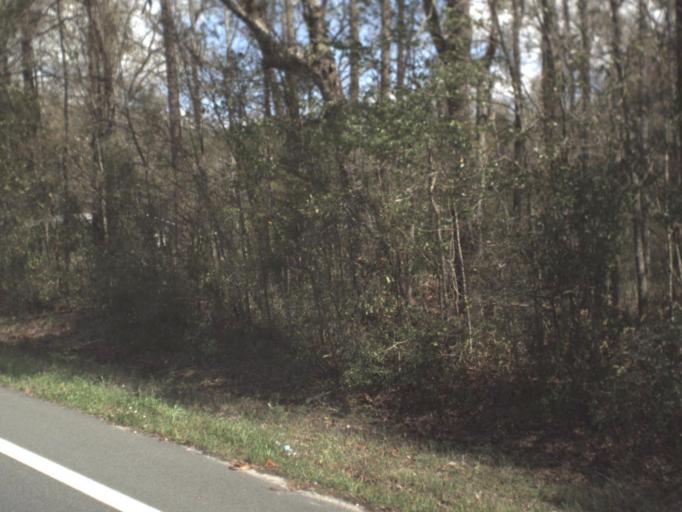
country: US
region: Florida
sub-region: Wakulla County
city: Crawfordville
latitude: 30.2373
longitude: -84.3624
